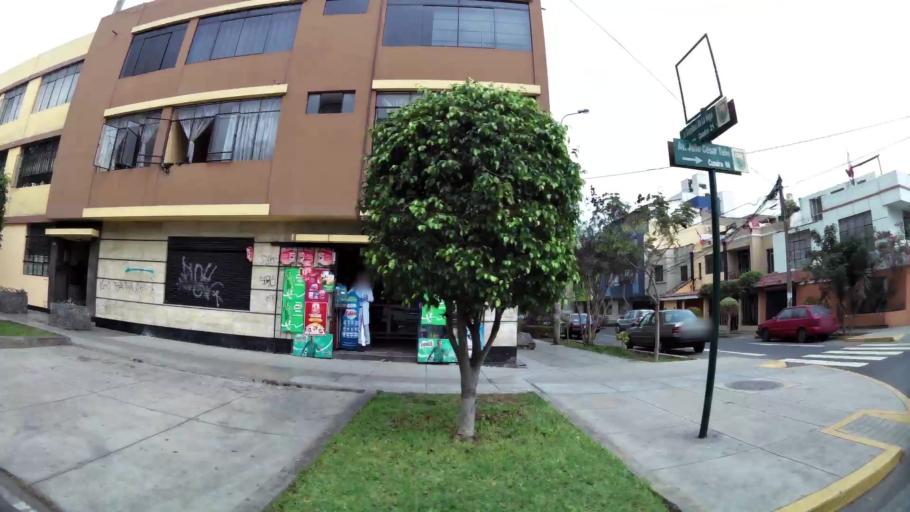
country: PE
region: Lima
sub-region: Lima
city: San Isidro
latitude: -12.0866
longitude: -77.0404
